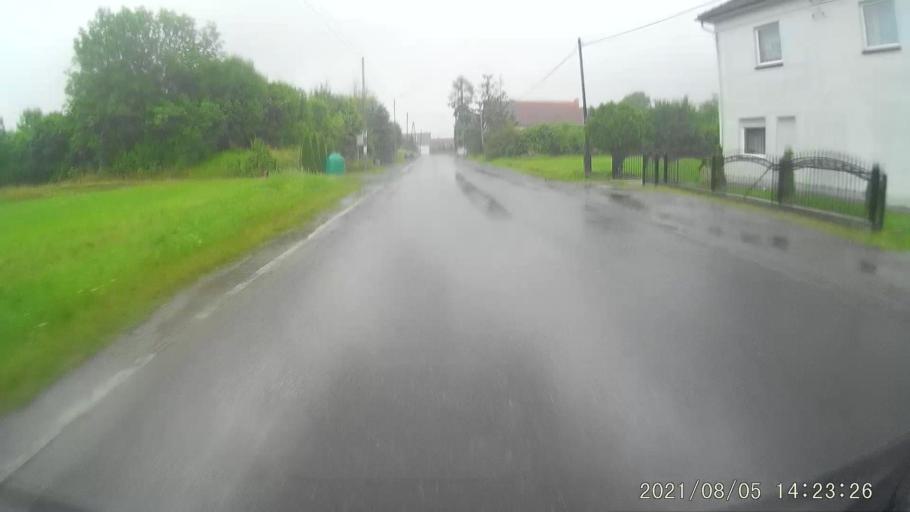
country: PL
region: Opole Voivodeship
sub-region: Powiat nyski
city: Korfantow
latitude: 50.4819
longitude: 17.6472
